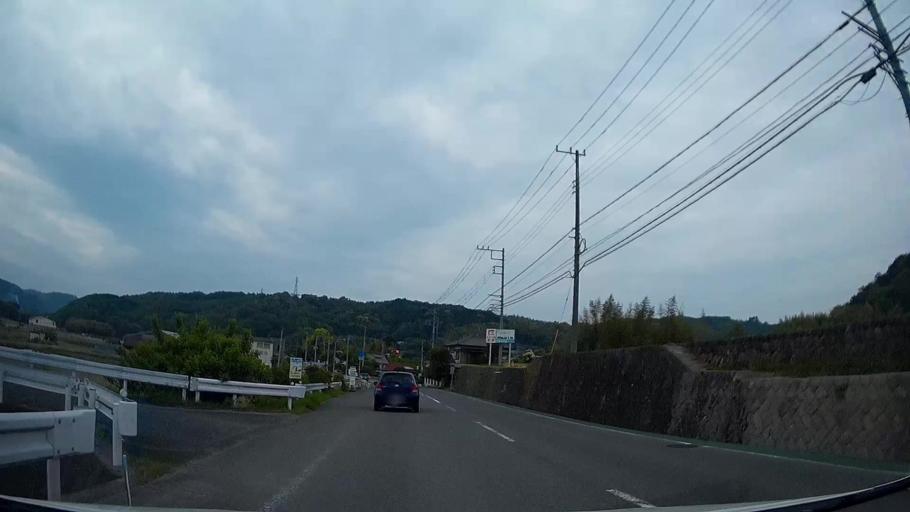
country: JP
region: Shizuoka
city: Ito
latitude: 34.9696
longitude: 138.9729
